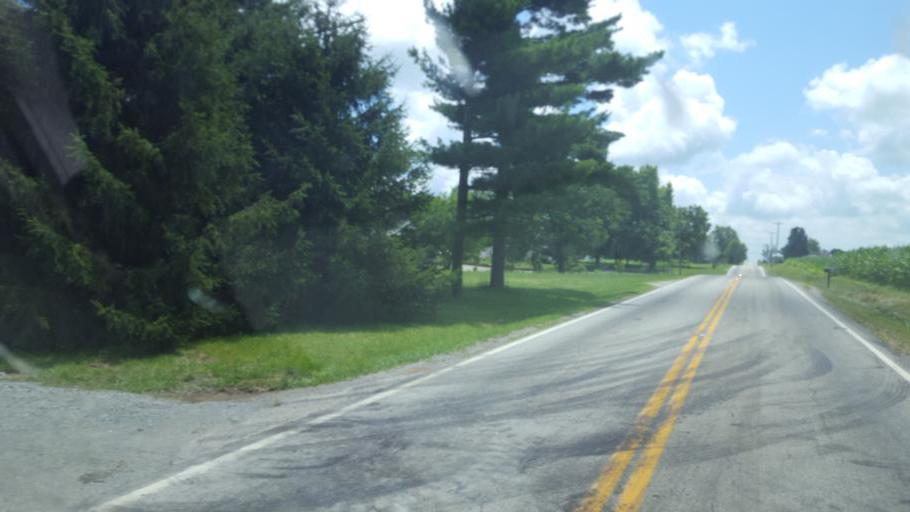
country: US
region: Ohio
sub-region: Highland County
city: Greenfield
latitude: 39.2398
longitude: -83.4315
